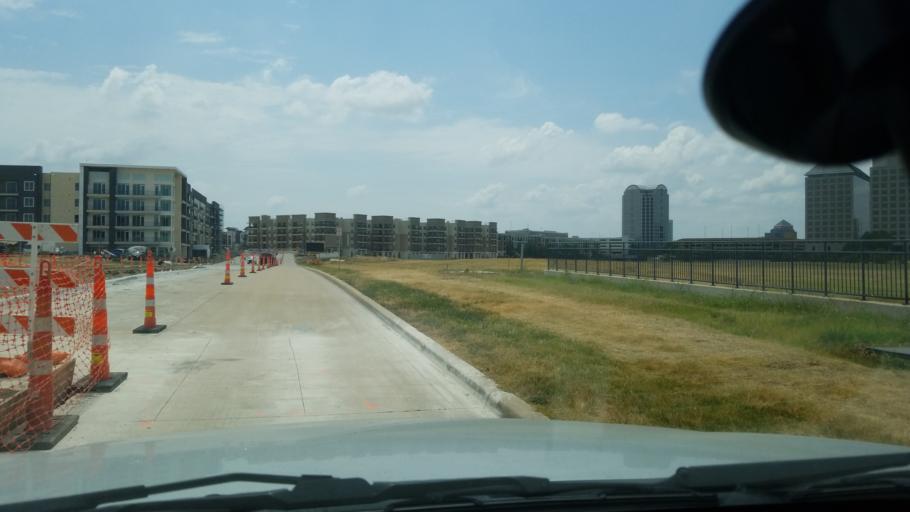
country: US
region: Texas
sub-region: Dallas County
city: Irving
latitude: 32.8757
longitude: -96.9396
